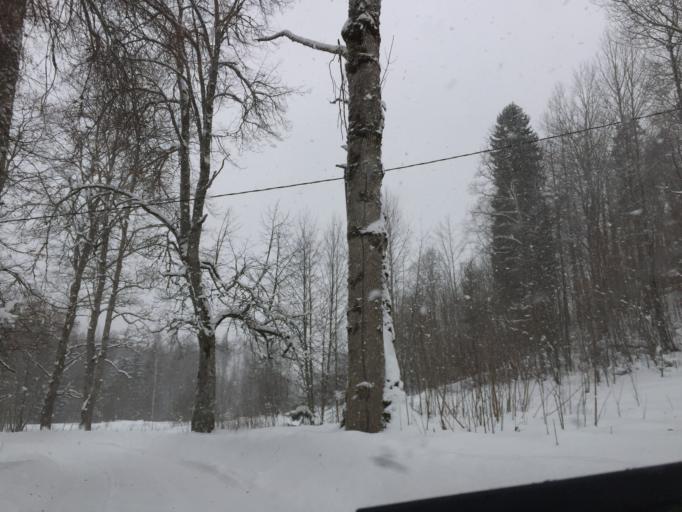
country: LV
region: Amatas Novads
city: Drabesi
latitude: 57.0836
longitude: 25.3903
